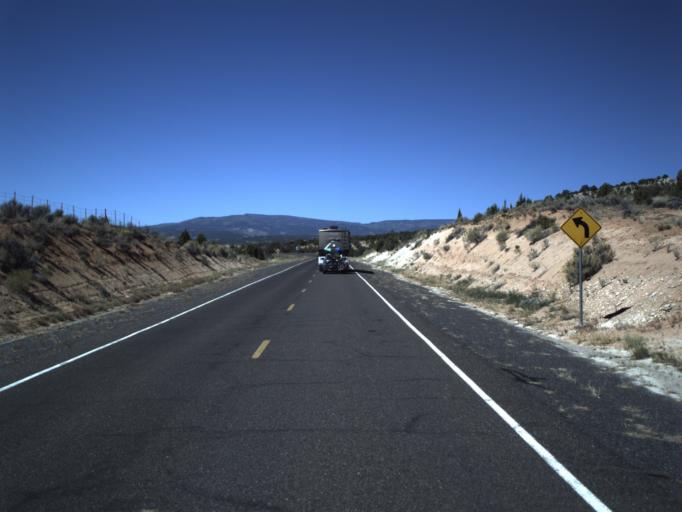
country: US
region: Utah
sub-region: Wayne County
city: Loa
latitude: 37.7535
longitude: -111.5686
